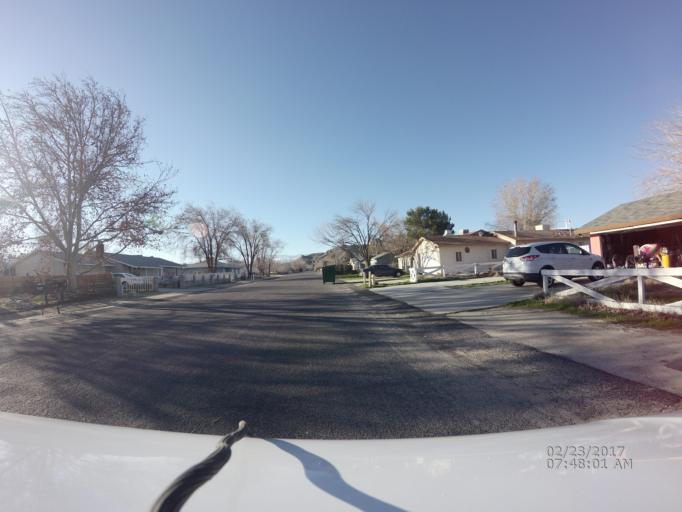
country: US
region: California
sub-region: Los Angeles County
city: Lake Los Angeles
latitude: 34.6144
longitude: -117.8138
